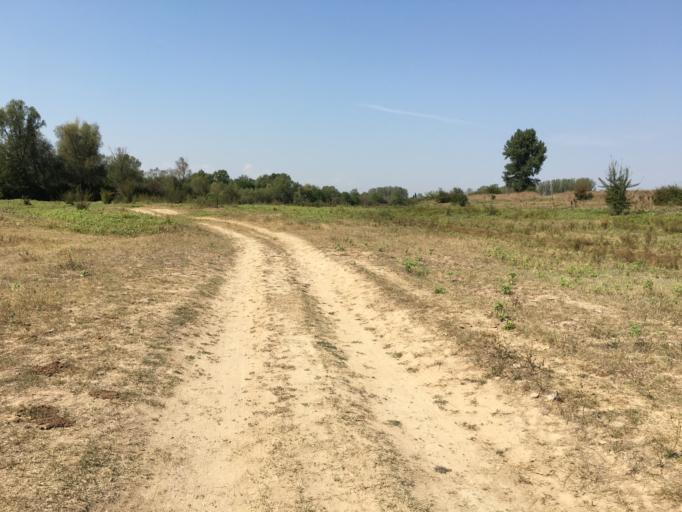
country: BG
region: Montana
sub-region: Obshtina Medkovets
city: Medkovets
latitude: 43.7209
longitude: 23.1571
